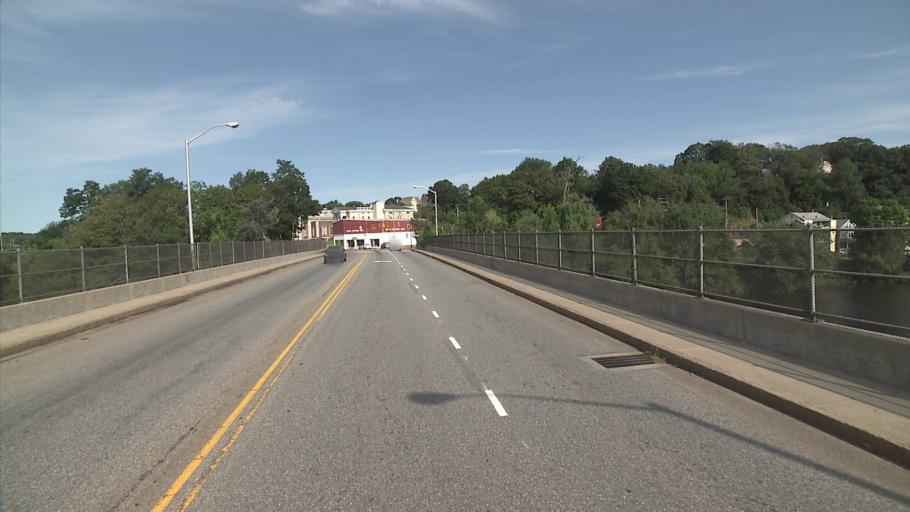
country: US
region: Connecticut
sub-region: New London County
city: Norwich
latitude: 41.5238
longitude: -72.0689
